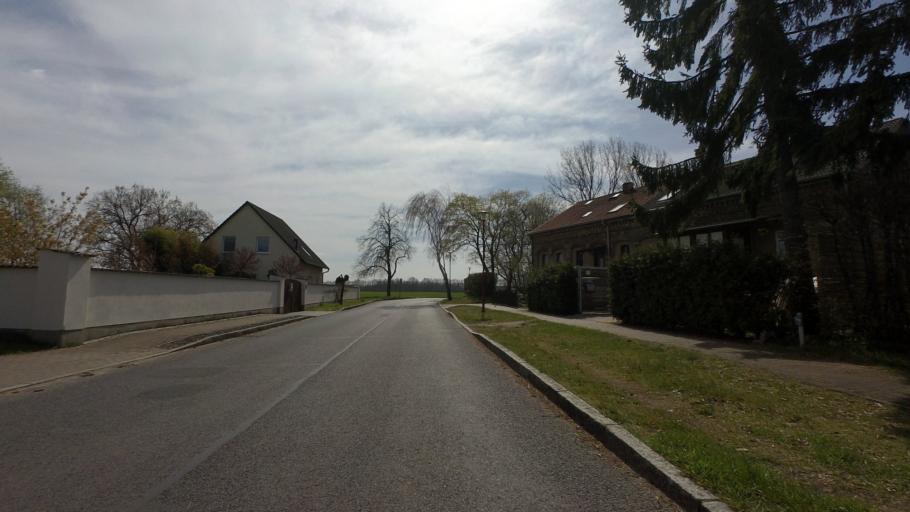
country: DE
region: Brandenburg
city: Ludwigsfelde
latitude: 52.3062
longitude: 13.1633
